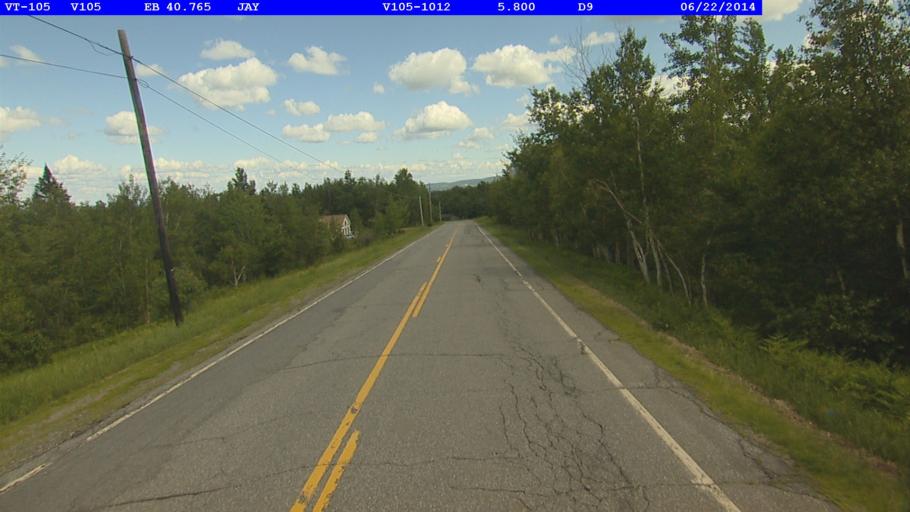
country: CA
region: Quebec
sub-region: Monteregie
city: Sutton
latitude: 44.9750
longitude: -72.4708
